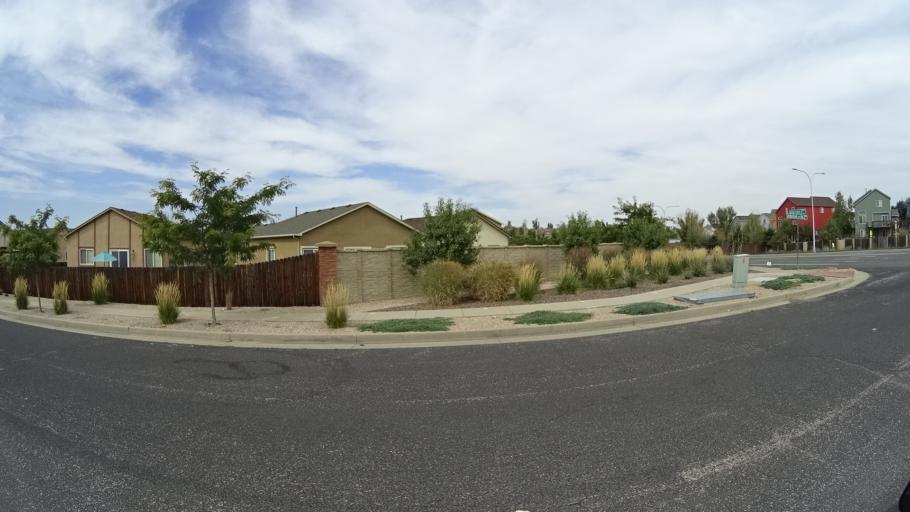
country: US
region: Colorado
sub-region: El Paso County
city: Cimarron Hills
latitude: 38.9046
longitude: -104.6971
